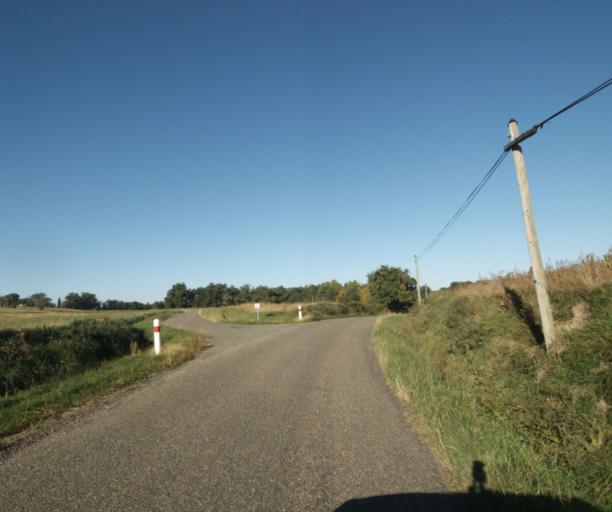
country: FR
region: Midi-Pyrenees
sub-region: Departement du Gers
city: Gondrin
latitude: 43.8494
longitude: 0.2290
